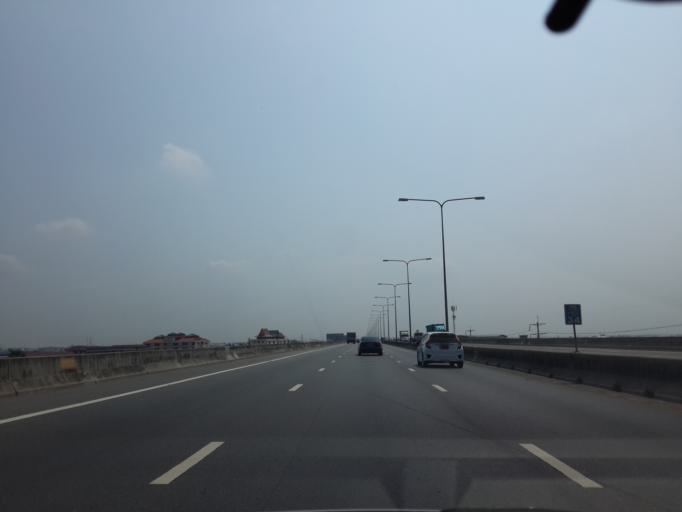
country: TH
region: Samut Prakan
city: Bang Bo
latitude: 13.5743
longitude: 100.9015
